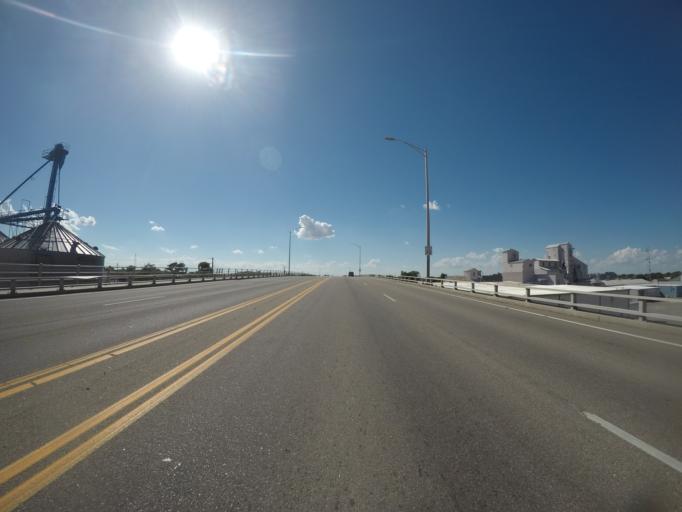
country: US
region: Colorado
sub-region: Logan County
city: Sterling
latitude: 40.6243
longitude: -103.2022
